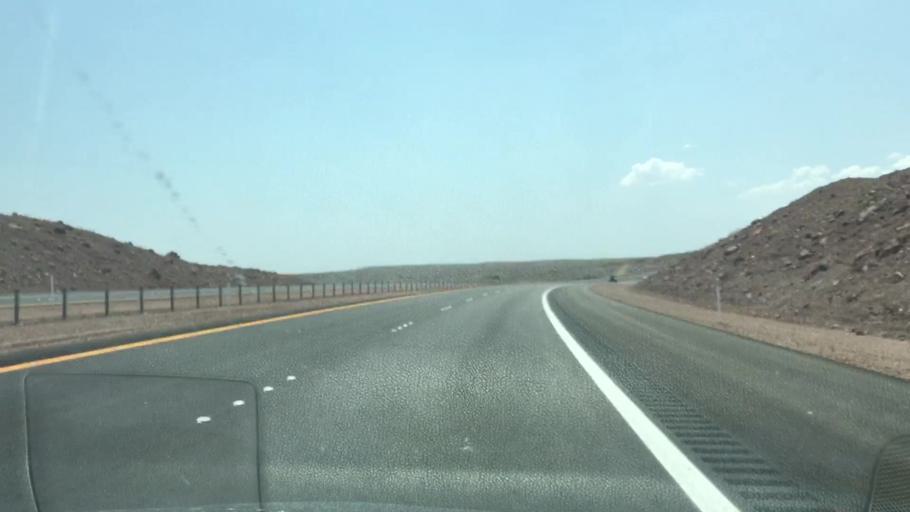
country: US
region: Nevada
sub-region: Clark County
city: Boulder City
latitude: 35.9773
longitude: -114.7924
